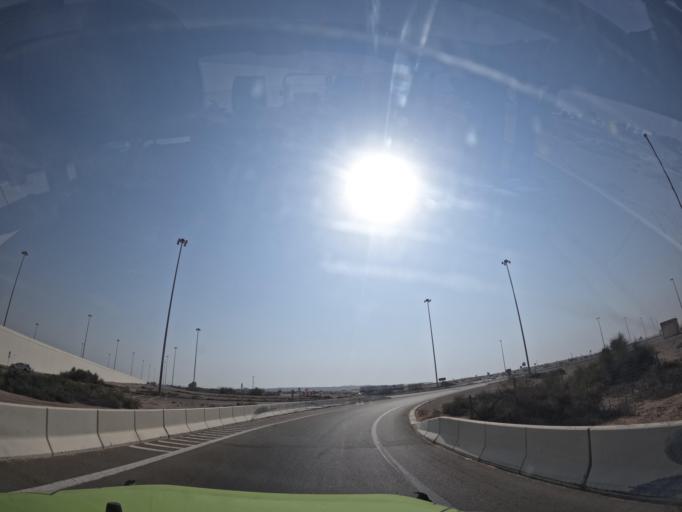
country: OM
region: Al Buraimi
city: Al Buraymi
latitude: 24.5253
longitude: 55.5522
